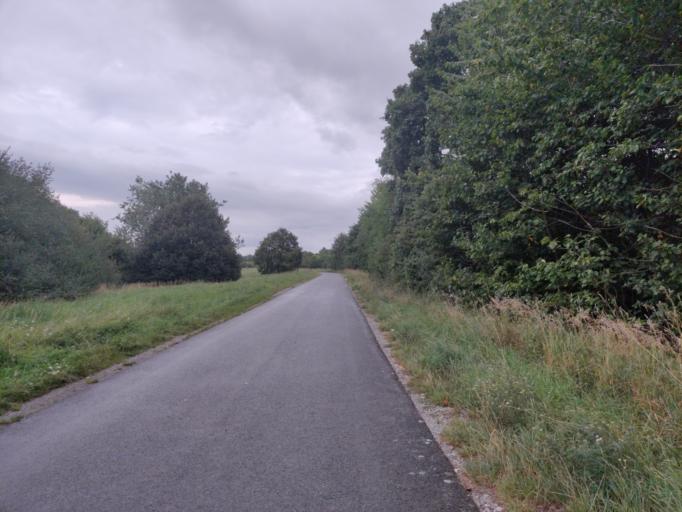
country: AT
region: Lower Austria
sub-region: Politischer Bezirk Korneuburg
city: Langenzersdorf
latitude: 48.2778
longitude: 16.3621
